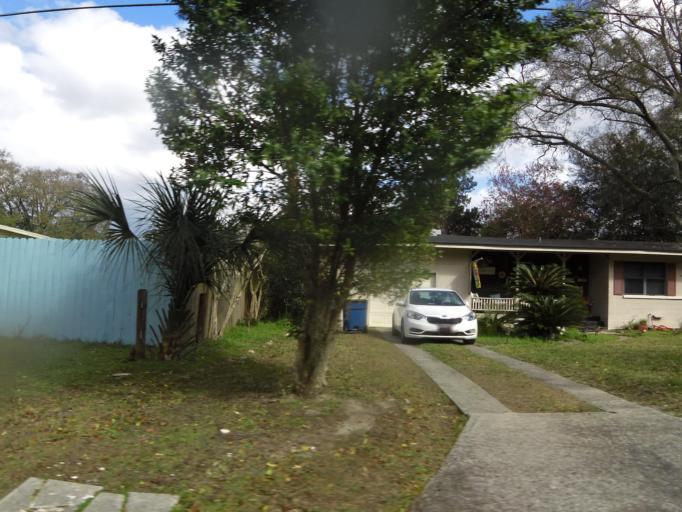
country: US
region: Florida
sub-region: Duval County
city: Jacksonville
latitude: 30.3398
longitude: -81.5983
